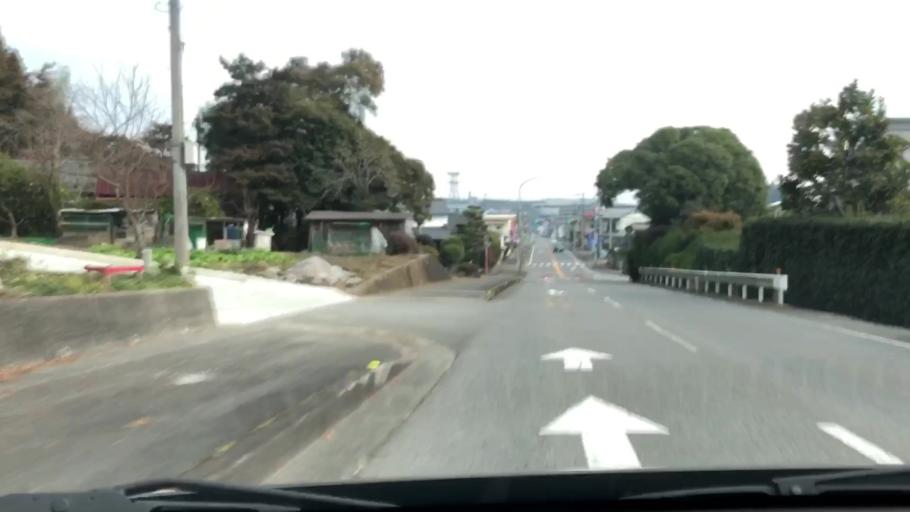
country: JP
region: Oita
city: Takedamachi
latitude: 32.9733
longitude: 131.5790
